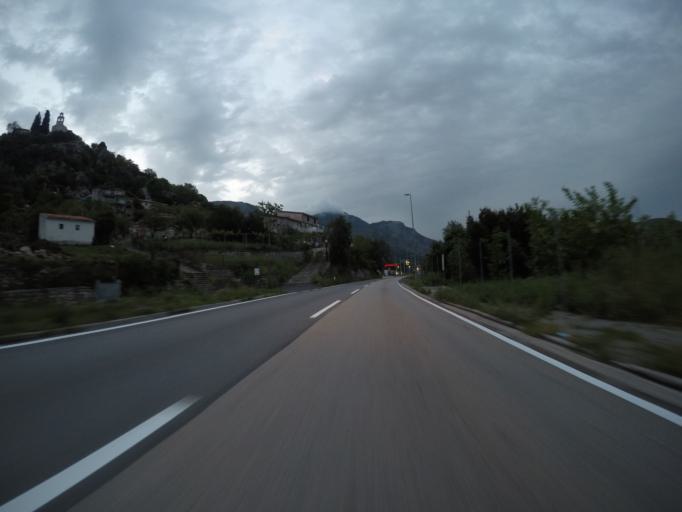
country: ME
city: Petrovac na Moru
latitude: 42.2013
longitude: 18.9622
